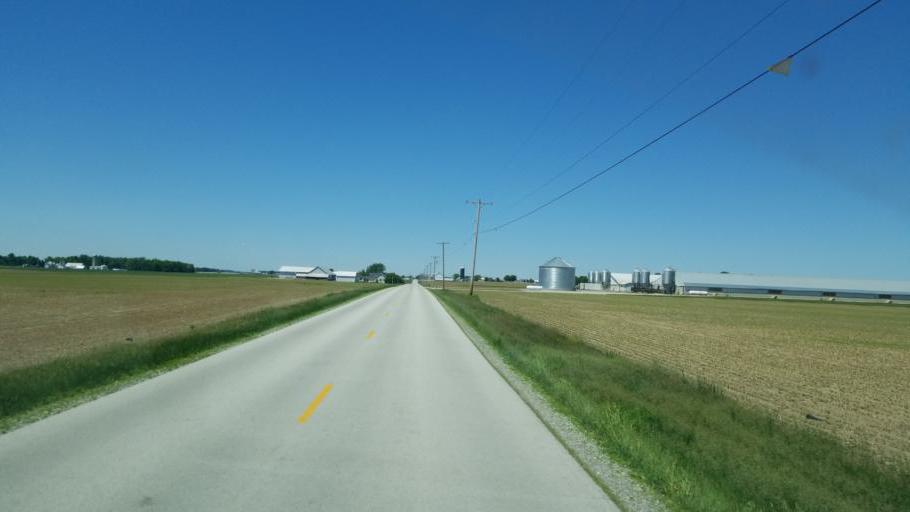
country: US
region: Ohio
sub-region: Auglaize County
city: Minster
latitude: 40.3856
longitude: -84.4199
